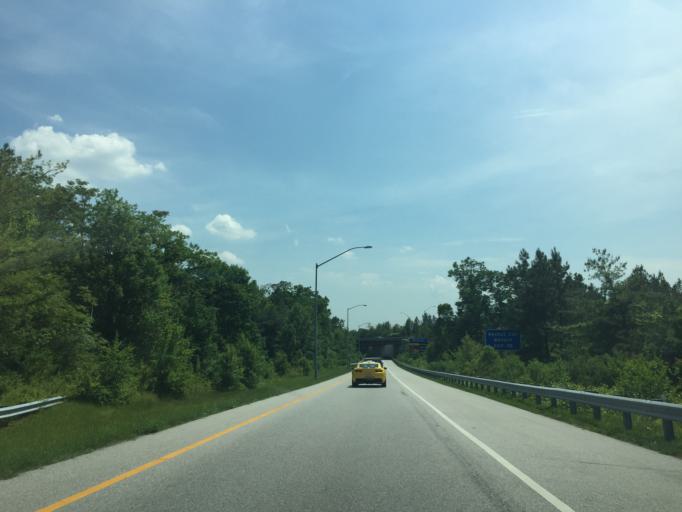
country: US
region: Maryland
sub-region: Howard County
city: Elkridge
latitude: 39.2008
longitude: -76.6920
